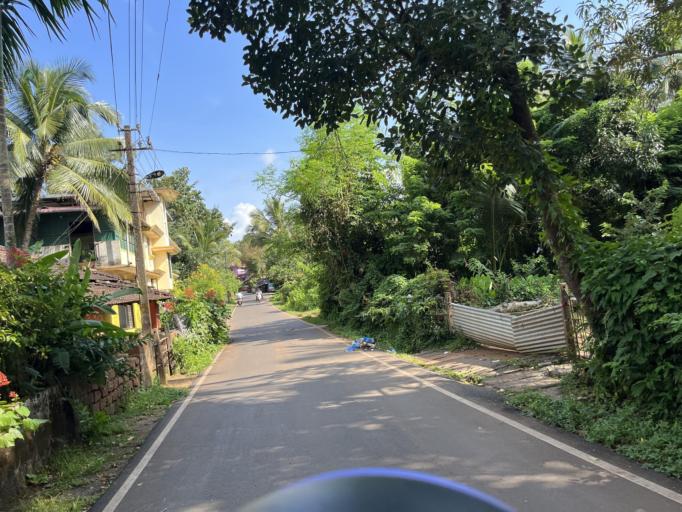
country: IN
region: Goa
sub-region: North Goa
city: Ponda
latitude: 15.3984
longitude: 74.0124
